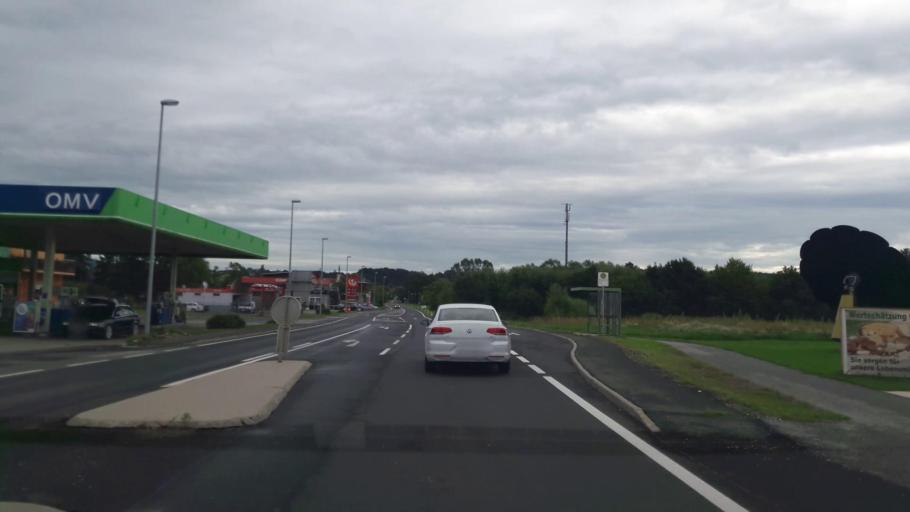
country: AT
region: Styria
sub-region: Politischer Bezirk Hartberg-Fuerstenfeld
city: Kaindorf
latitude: 47.2187
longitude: 15.9013
